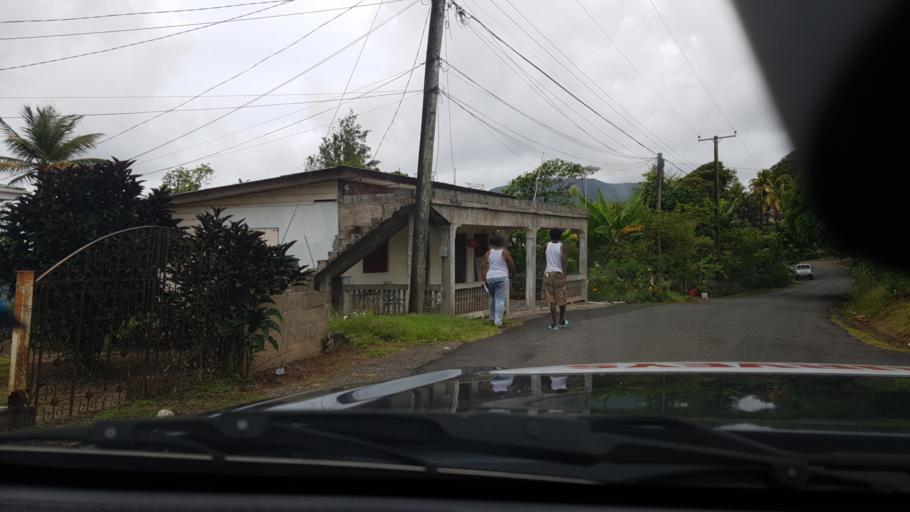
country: LC
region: Castries Quarter
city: Bisee
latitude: 14.0111
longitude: -60.9383
